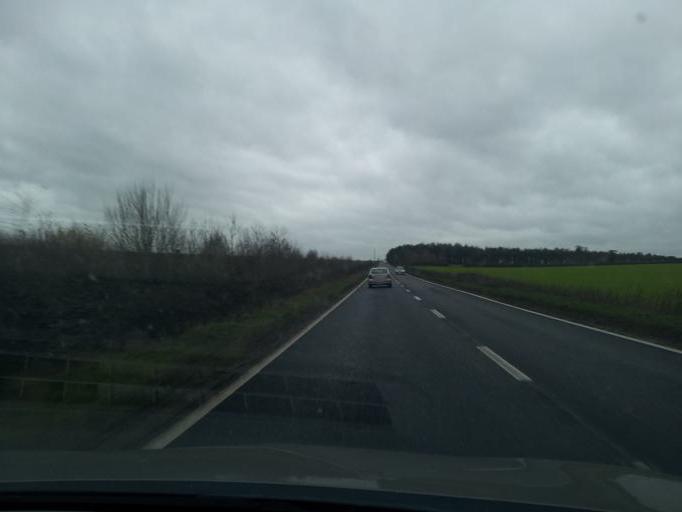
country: GB
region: England
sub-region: Suffolk
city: Ixworth
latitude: 52.2865
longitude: 0.8159
